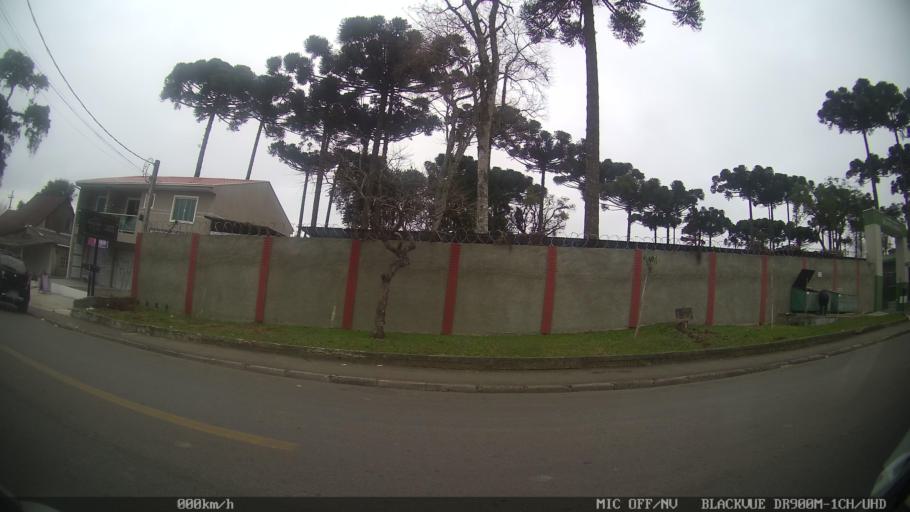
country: BR
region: Parana
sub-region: Almirante Tamandare
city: Almirante Tamandare
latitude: -25.3730
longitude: -49.3297
